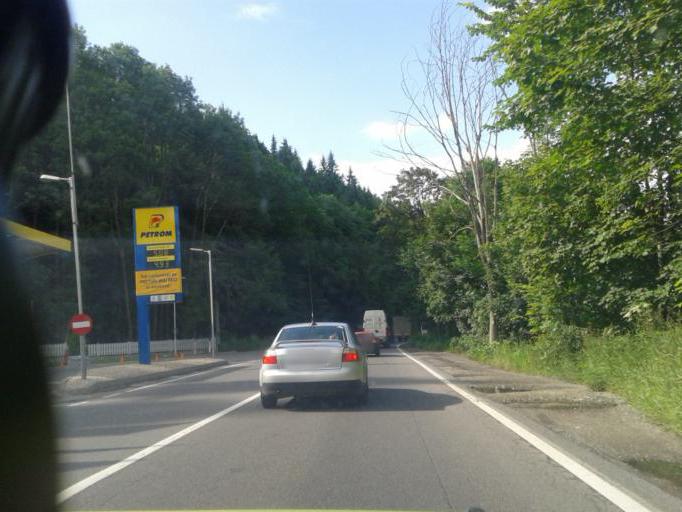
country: RO
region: Prahova
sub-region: Oras Busteni
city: Poiana Tapului
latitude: 45.3837
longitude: 25.5376
